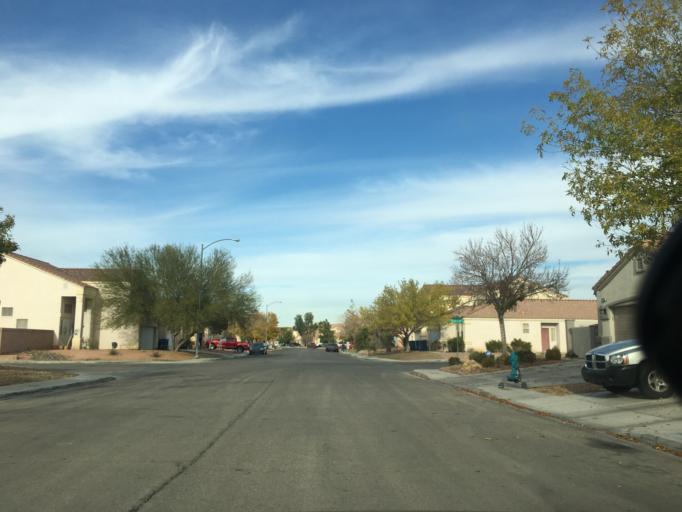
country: US
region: Nevada
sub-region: Clark County
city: Enterprise
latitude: 36.0146
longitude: -115.1671
